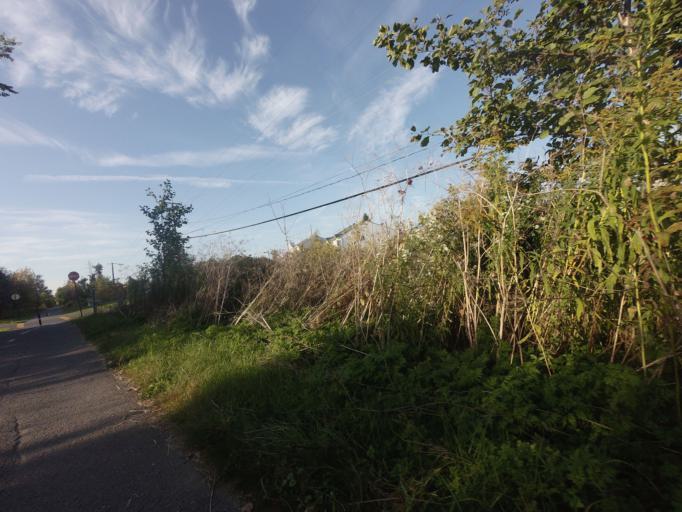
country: CA
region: Quebec
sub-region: Laurentides
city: Saint-Jerome
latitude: 45.8003
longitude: -74.0053
